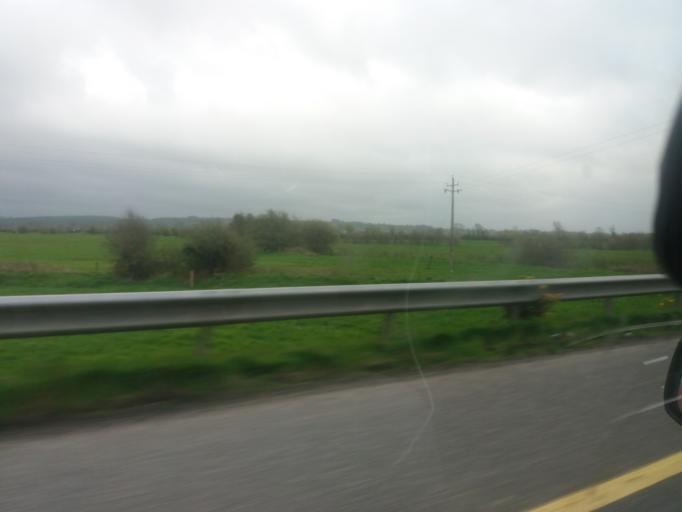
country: IE
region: Munster
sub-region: County Limerick
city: Rathkeale
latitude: 52.4919
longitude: -9.0008
